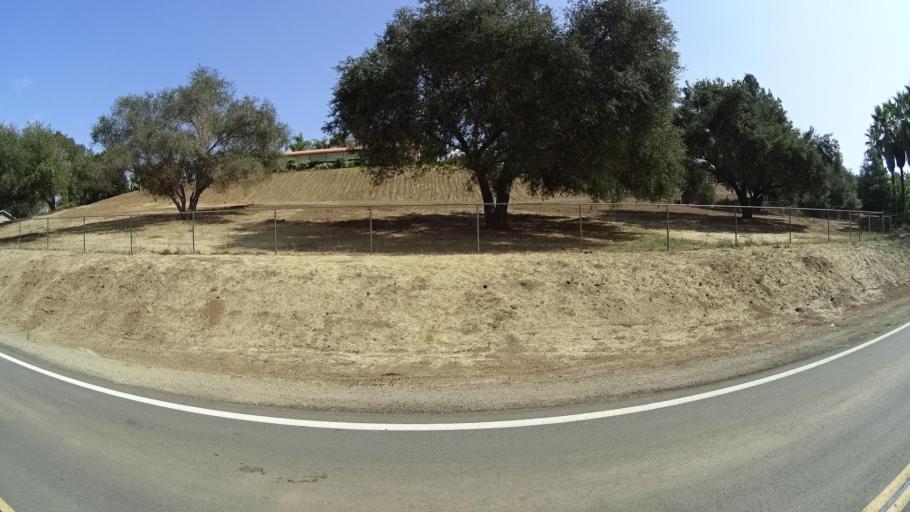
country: US
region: California
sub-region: San Diego County
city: Escondido
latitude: 33.1106
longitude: -117.0475
